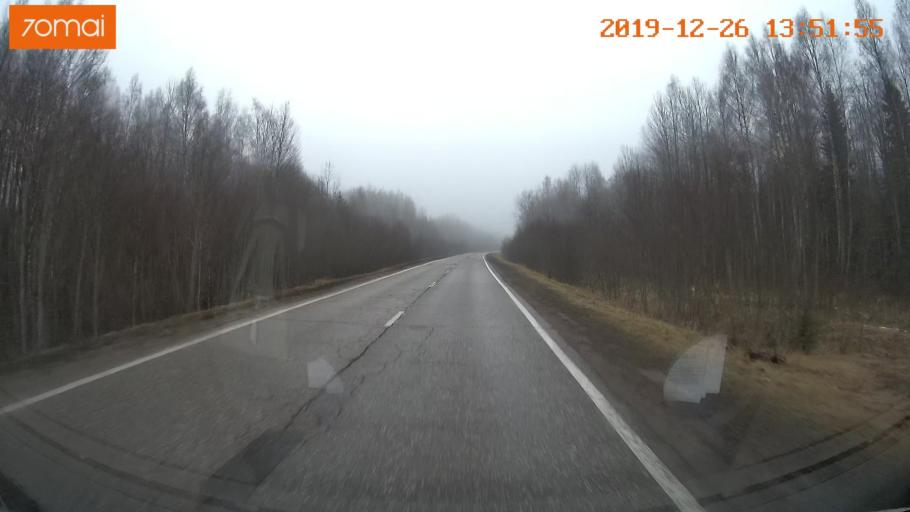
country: RU
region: Jaroslavl
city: Poshekhon'ye
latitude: 58.6384
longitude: 38.5964
